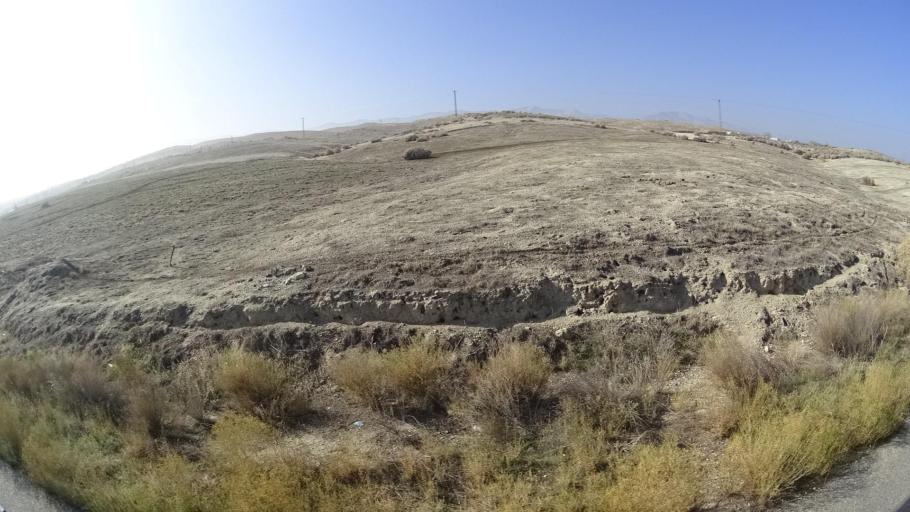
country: US
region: California
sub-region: Kern County
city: Taft Heights
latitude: 35.1711
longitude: -119.5347
